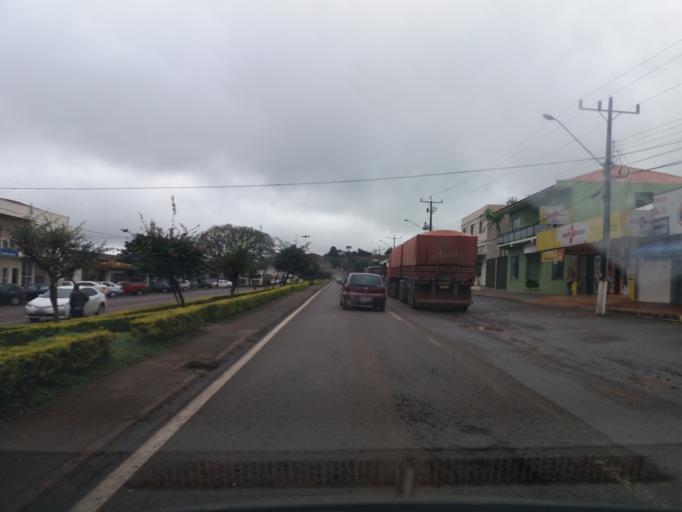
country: BR
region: Parana
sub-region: Cascavel
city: Cascavel
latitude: -25.2603
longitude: -53.5758
